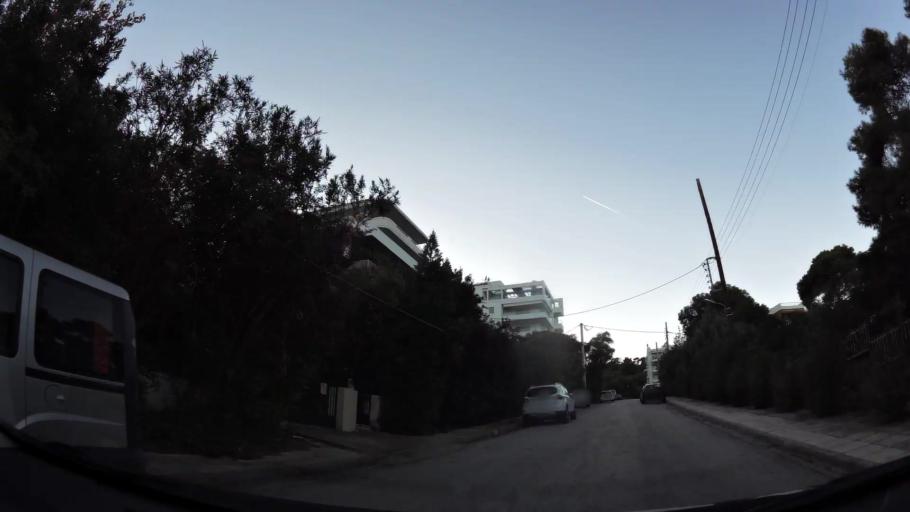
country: GR
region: Attica
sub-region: Nomarchia Anatolikis Attikis
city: Vouliagmeni
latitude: 37.8122
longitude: 23.7983
